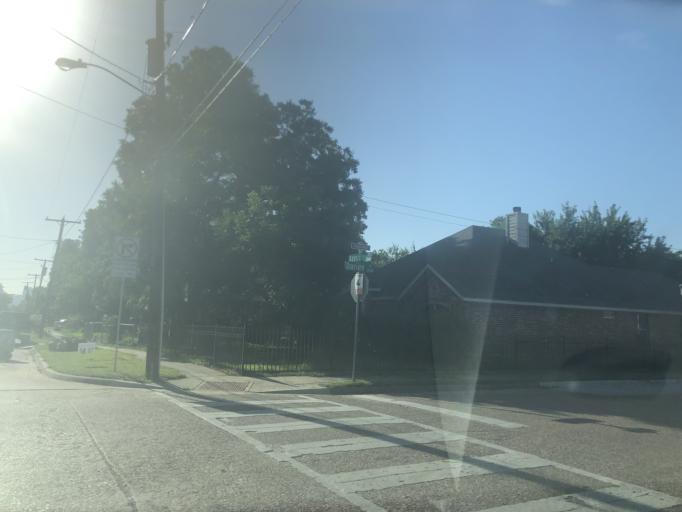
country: US
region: Texas
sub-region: Dallas County
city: Dallas
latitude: 32.7887
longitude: -96.8521
